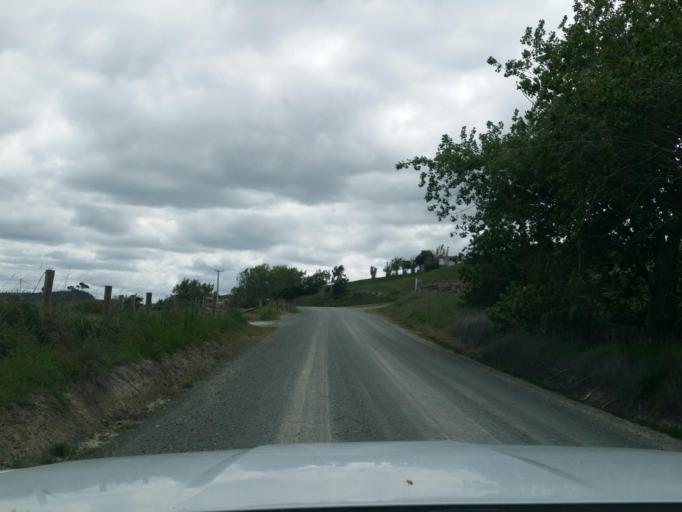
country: NZ
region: Auckland
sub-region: Auckland
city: Wellsford
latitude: -36.2712
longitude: 174.3710
